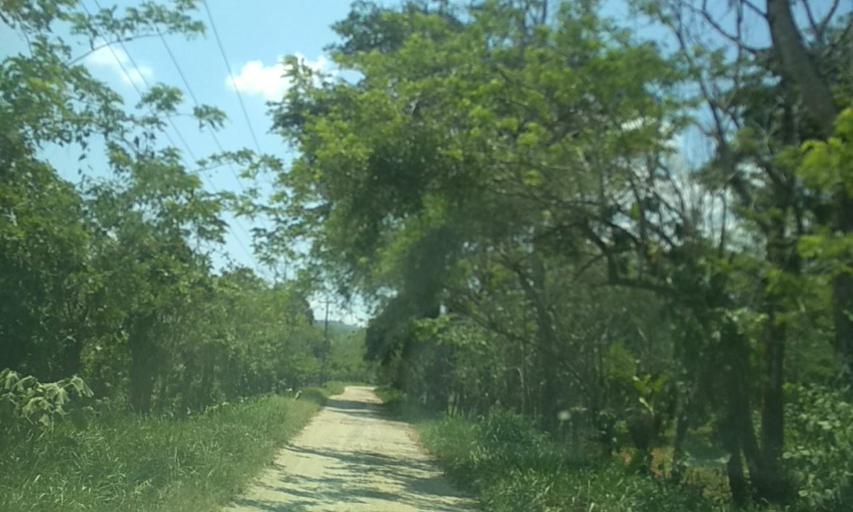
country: MX
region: Chiapas
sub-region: Tecpatan
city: Raudales Malpaso
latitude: 17.2837
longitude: -93.8338
